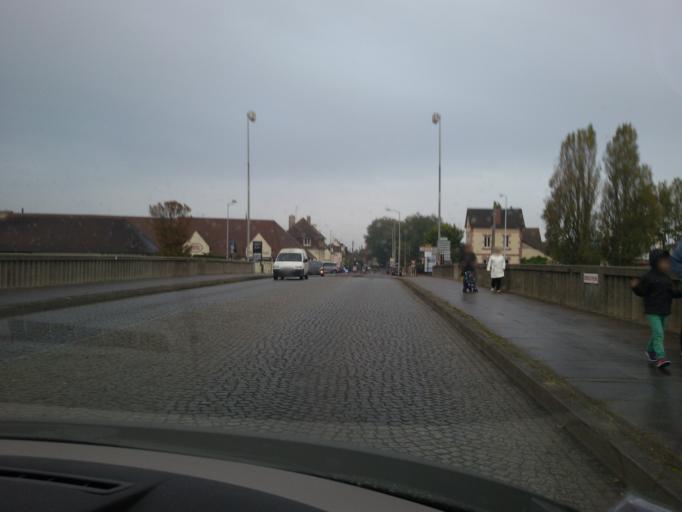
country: FR
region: Lower Normandy
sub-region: Departement du Calvados
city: Cabourg
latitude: 49.2857
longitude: -0.1115
